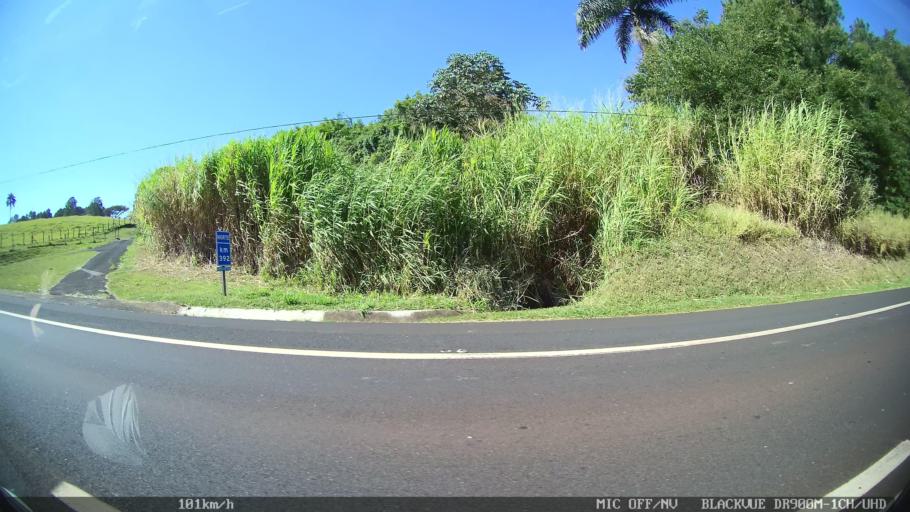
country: BR
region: Sao Paulo
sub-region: Franca
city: Franca
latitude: -20.5807
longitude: -47.4280
